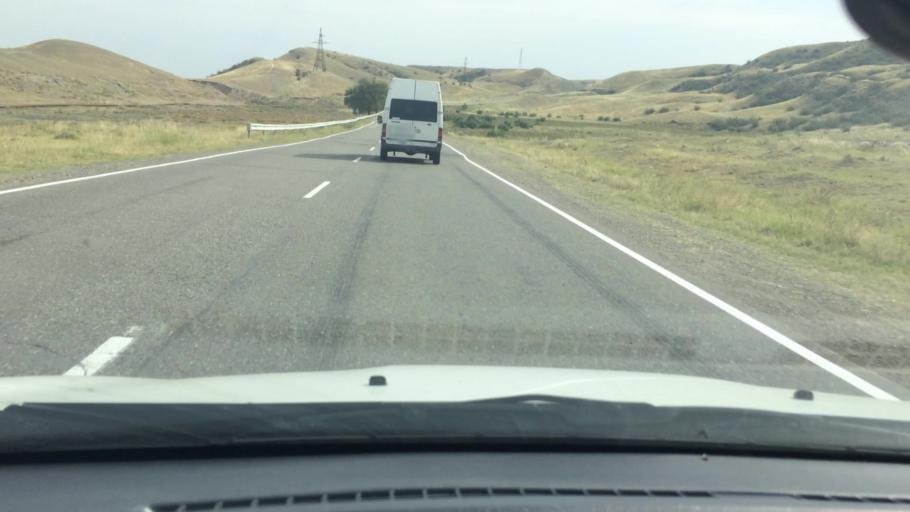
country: GE
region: Kvemo Kartli
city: Rust'avi
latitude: 41.5309
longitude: 44.9847
